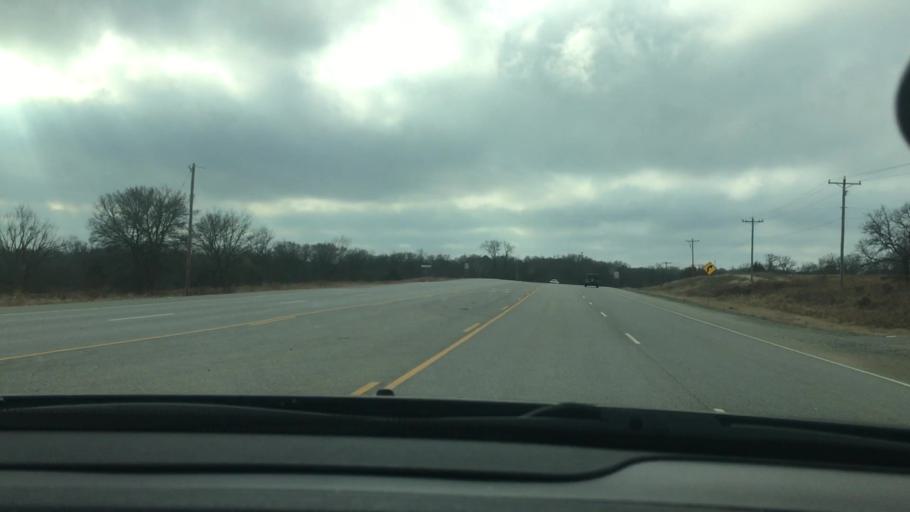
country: US
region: Oklahoma
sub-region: Bryan County
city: Durant
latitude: 34.0522
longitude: -96.3729
